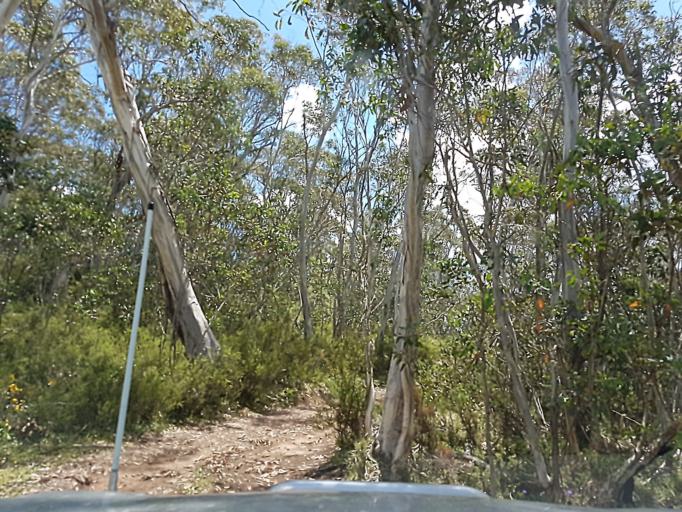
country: AU
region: New South Wales
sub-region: Snowy River
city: Jindabyne
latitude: -36.9193
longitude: 148.1327
